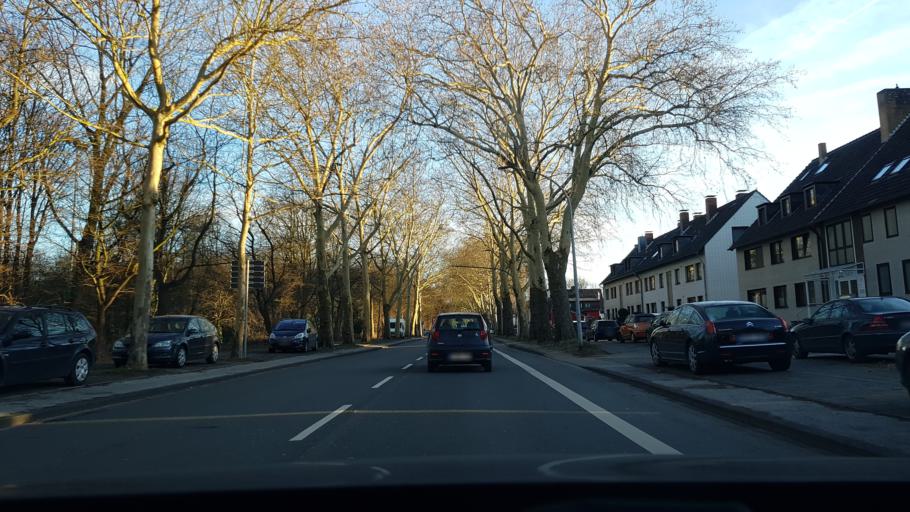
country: DE
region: North Rhine-Westphalia
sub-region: Regierungsbezirk Dusseldorf
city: Hochfeld
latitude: 51.4031
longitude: 6.7798
